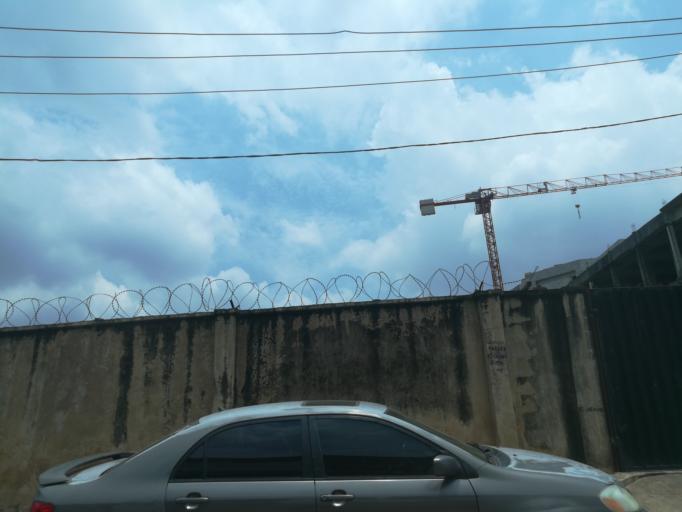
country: NG
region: Lagos
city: Ojota
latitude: 6.5939
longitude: 3.3684
